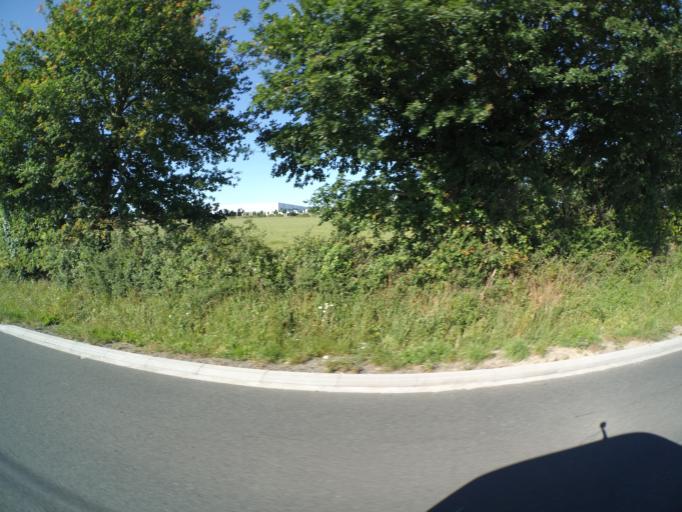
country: FR
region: Pays de la Loire
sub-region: Departement de la Vendee
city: Les Herbiers
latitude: 46.8897
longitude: -1.0470
